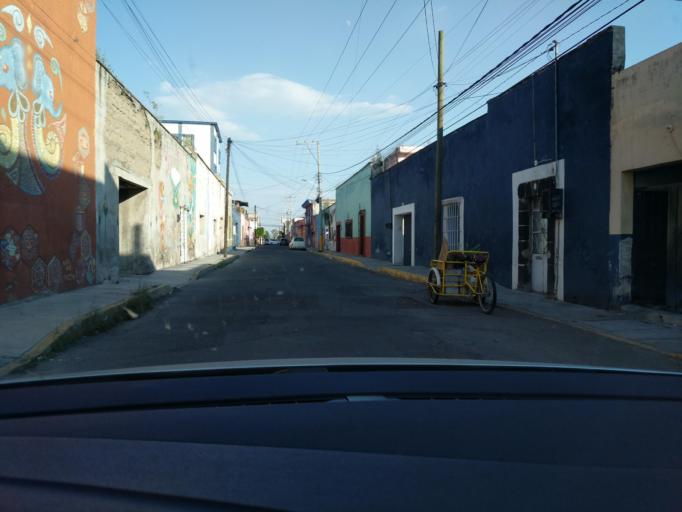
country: MX
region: Puebla
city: Cholula
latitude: 19.0574
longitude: -98.3108
